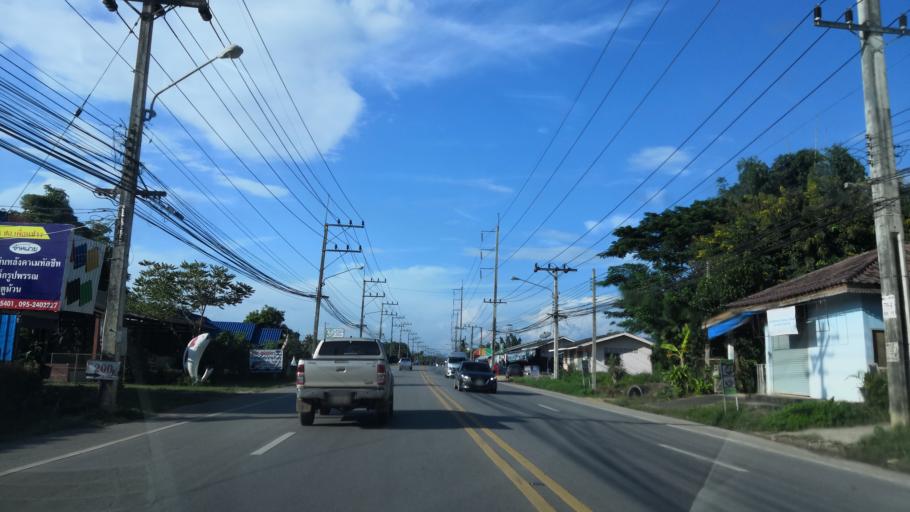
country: TH
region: Chiang Rai
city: Wiang Pa Pao
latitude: 19.3077
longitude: 99.5117
